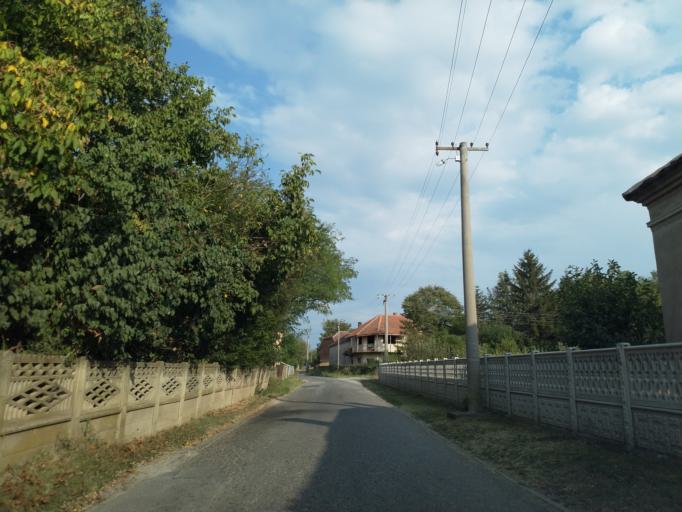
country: RS
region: Central Serbia
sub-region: Pomoravski Okrug
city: Paracin
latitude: 43.8444
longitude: 21.4806
